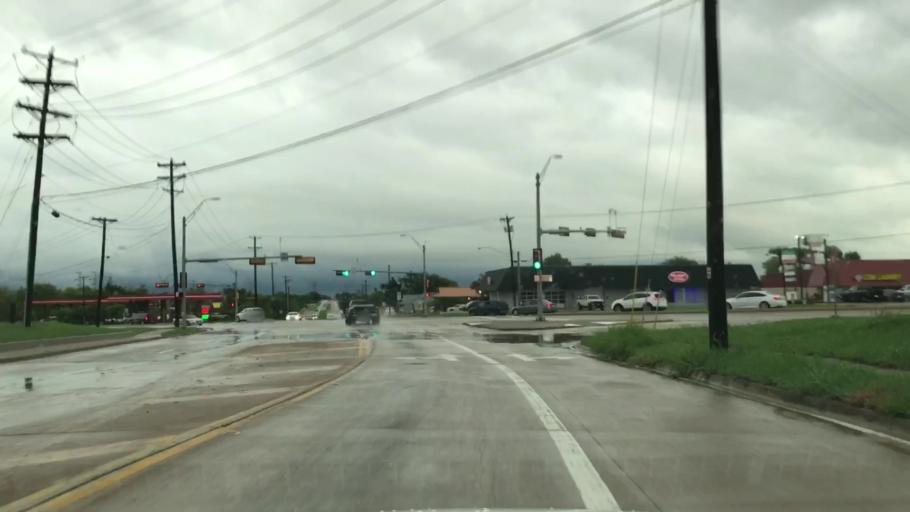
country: US
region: Texas
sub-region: Collin County
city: Wylie
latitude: 33.0172
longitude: -96.5326
